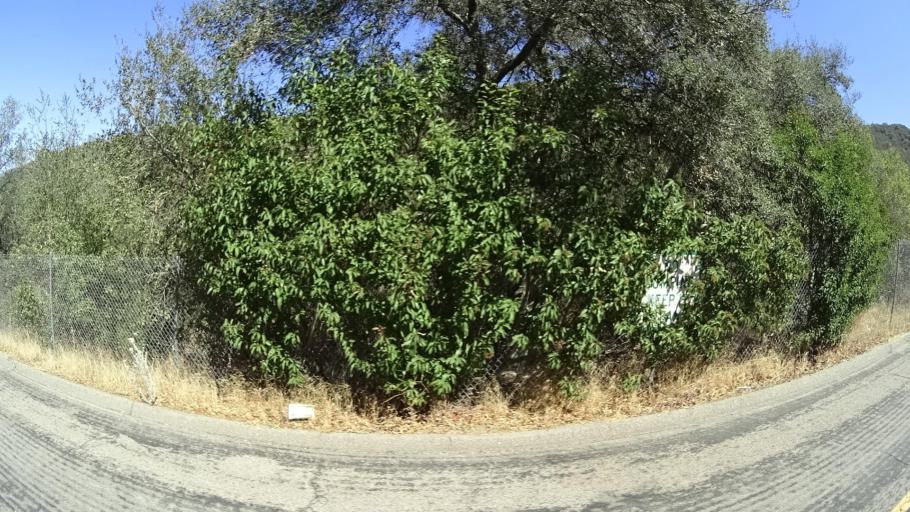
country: US
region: California
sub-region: San Diego County
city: Rainbow
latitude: 33.3326
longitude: -117.0857
